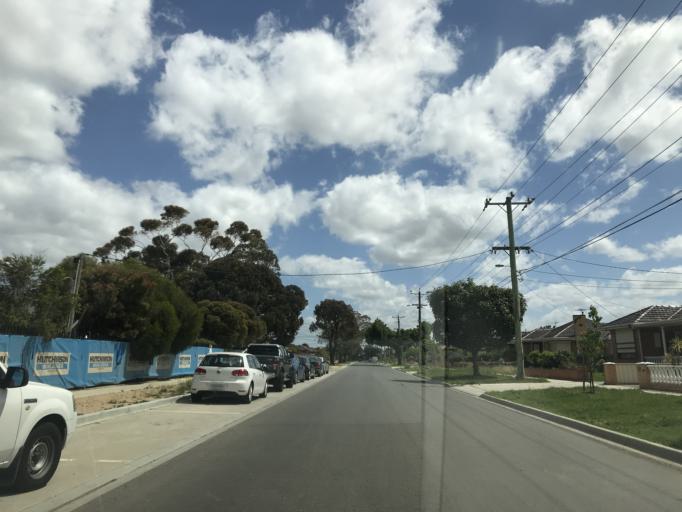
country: AU
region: Victoria
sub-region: Brimbank
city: Sunshine West
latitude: -37.7925
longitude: 144.8135
